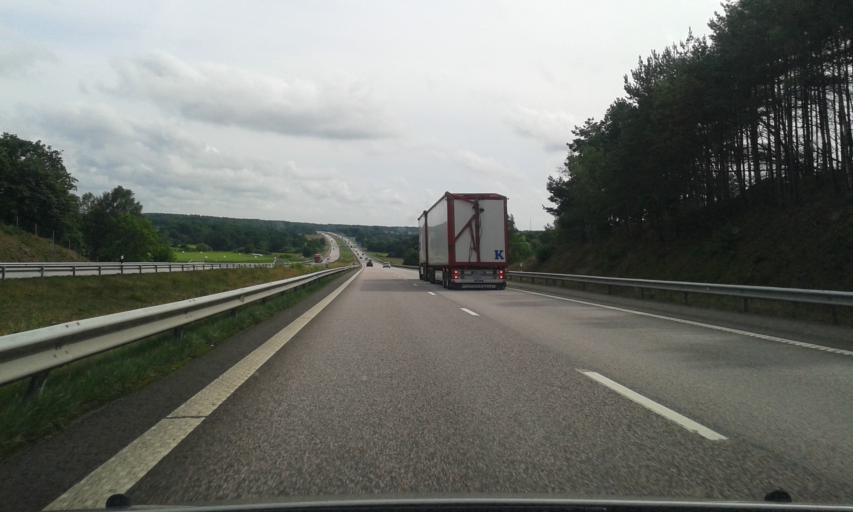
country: SE
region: Halland
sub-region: Kungsbacka Kommun
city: Frillesas
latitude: 57.2689
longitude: 12.2153
